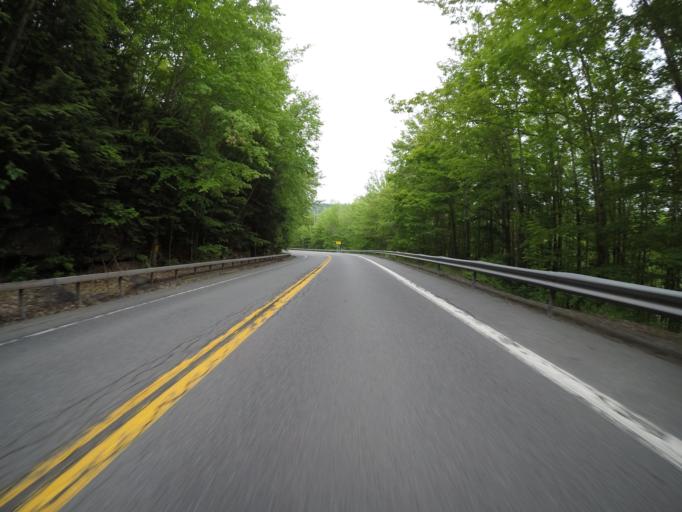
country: US
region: New York
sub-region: Sullivan County
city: Livingston Manor
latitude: 42.0907
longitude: -74.8333
